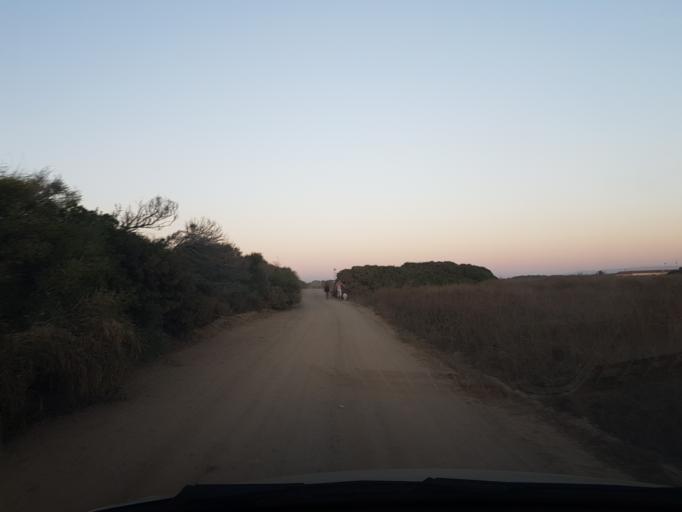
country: IT
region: Sardinia
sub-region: Provincia di Oristano
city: Riola Sardo
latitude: 40.0410
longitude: 8.3991
